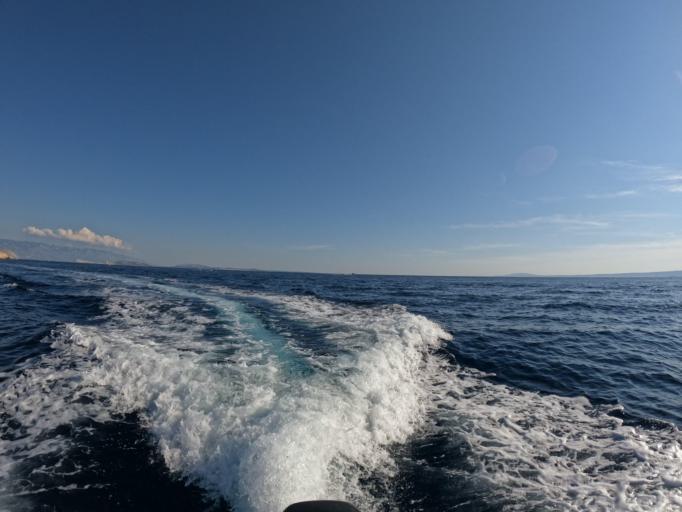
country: HR
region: Primorsko-Goranska
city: Punat
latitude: 44.9707
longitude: 14.6343
